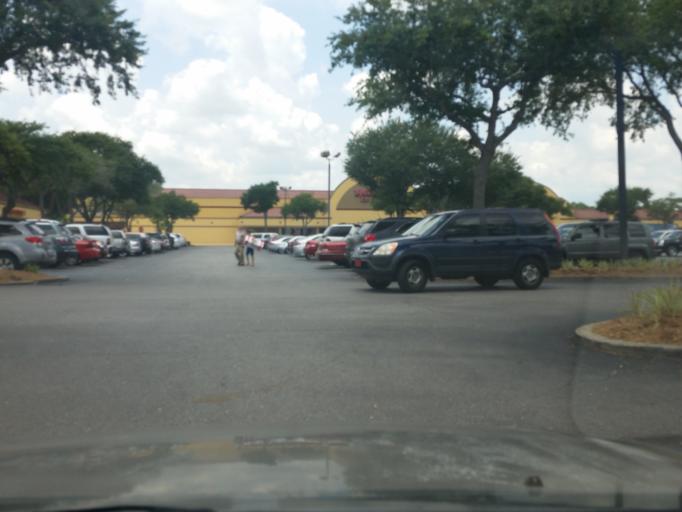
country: US
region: Florida
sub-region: Escambia County
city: Ferry Pass
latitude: 30.4928
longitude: -87.2251
